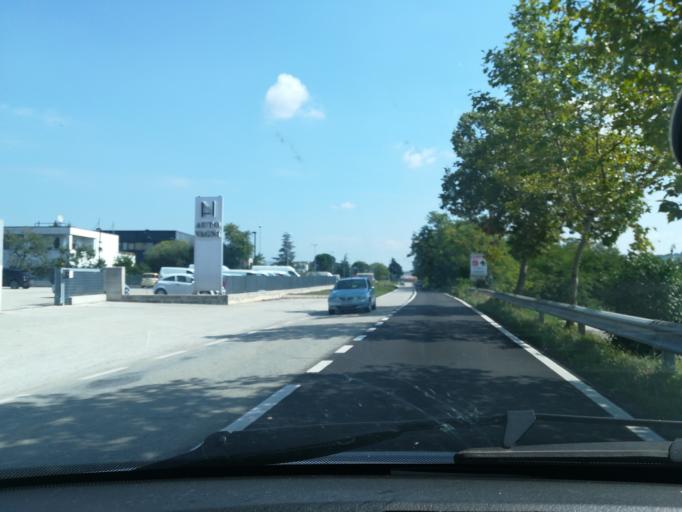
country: IT
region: The Marches
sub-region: Provincia di Macerata
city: Tolentino
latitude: 43.2208
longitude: 13.3238
